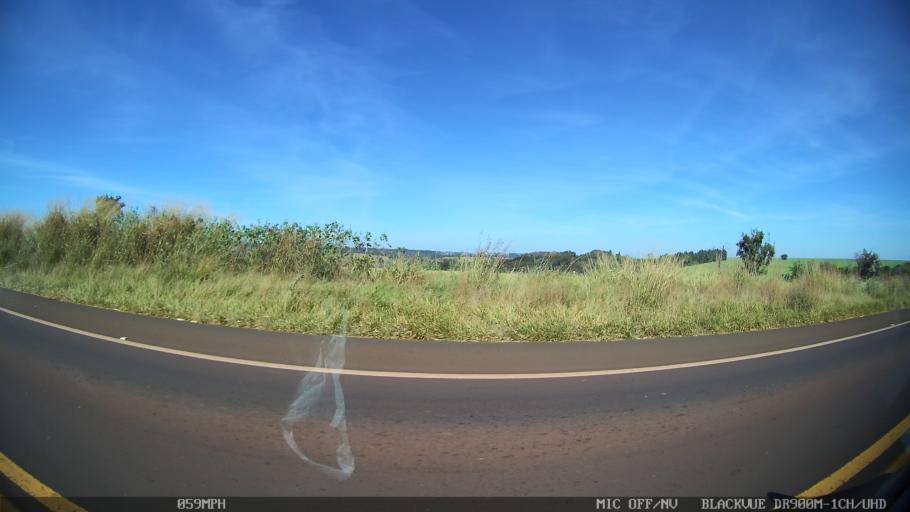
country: BR
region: Sao Paulo
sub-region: Franca
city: Franca
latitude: -20.5551
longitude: -47.4949
